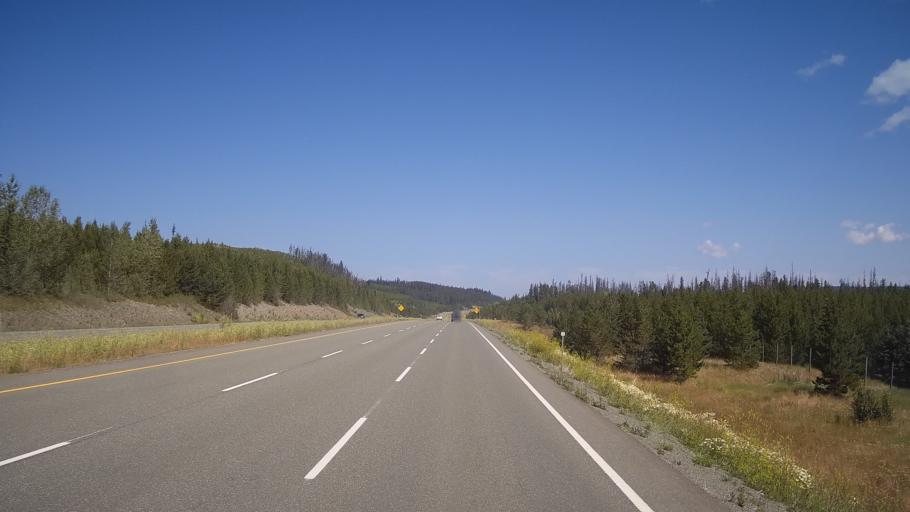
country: CA
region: British Columbia
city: Logan Lake
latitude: 50.3550
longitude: -120.6265
